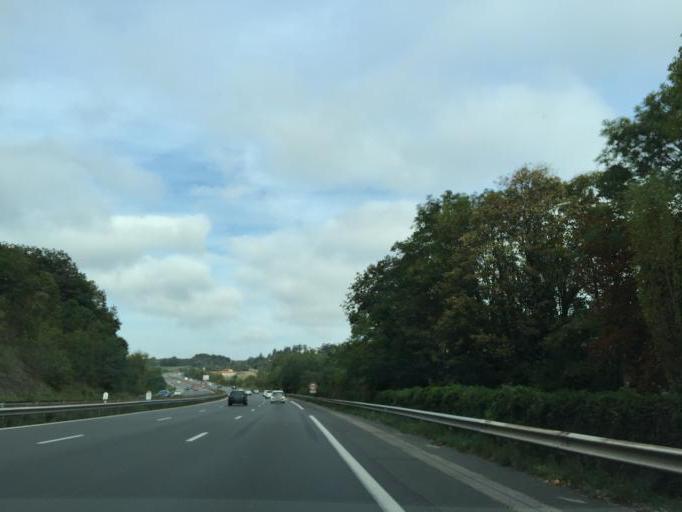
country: FR
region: Rhone-Alpes
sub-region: Departement de la Loire
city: La Fouillouse
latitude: 45.4995
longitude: 4.3119
